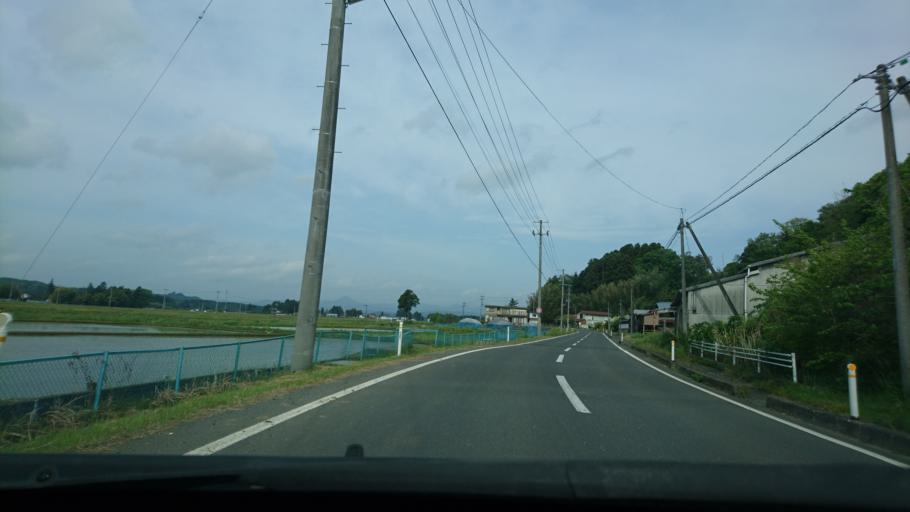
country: JP
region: Iwate
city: Ichinoseki
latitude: 38.8214
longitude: 141.0399
